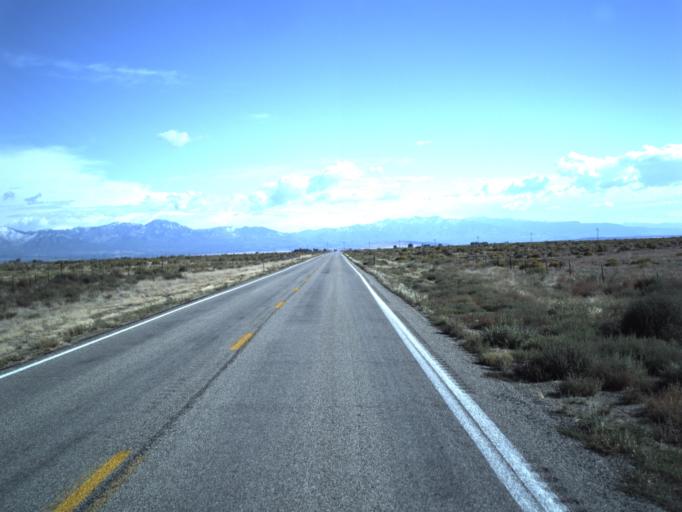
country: US
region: Utah
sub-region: Millard County
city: Delta
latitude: 39.2386
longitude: -112.4319
